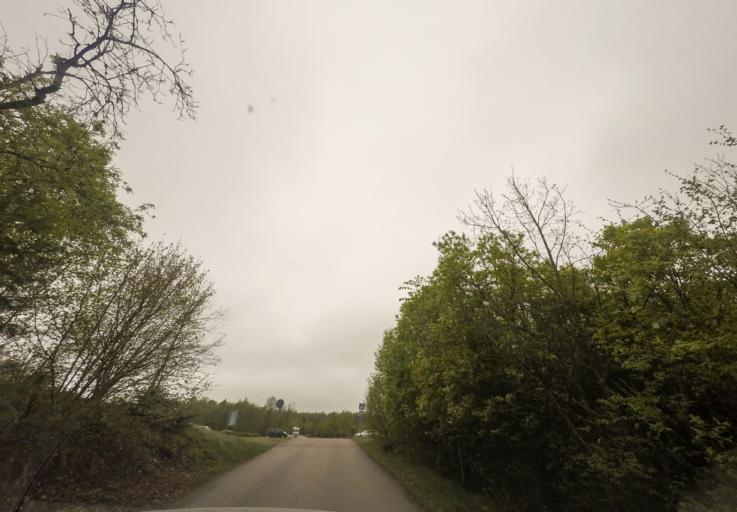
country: SE
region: Vaestmanland
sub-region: Vasteras
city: Vasteras
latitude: 59.5675
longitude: 16.6224
